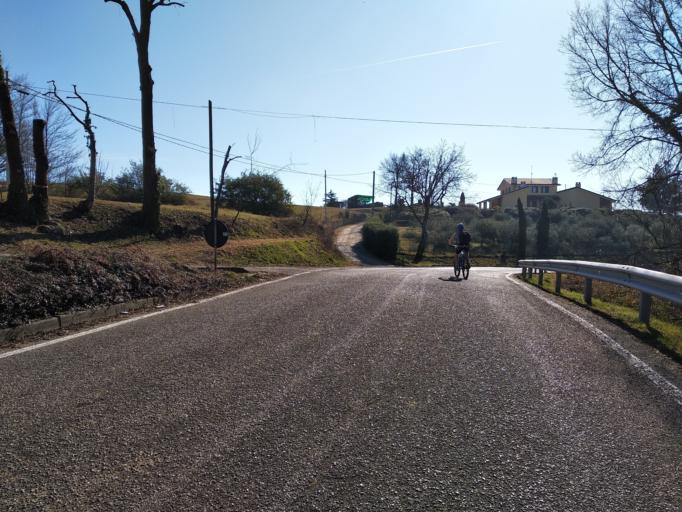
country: IT
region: Veneto
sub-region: Provincia di Vicenza
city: Gambugliano
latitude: 45.5872
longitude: 11.4554
